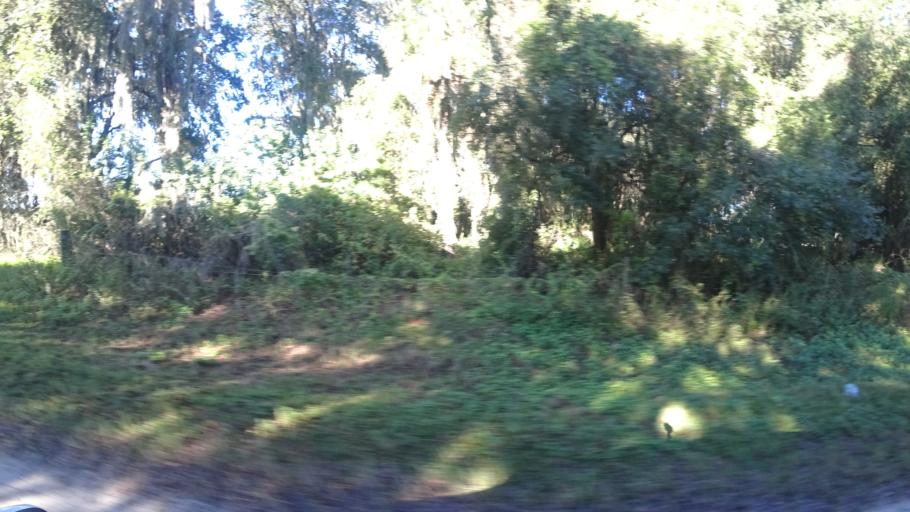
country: US
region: Florida
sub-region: Hillsborough County
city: Ruskin
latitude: 27.6399
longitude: -82.4172
